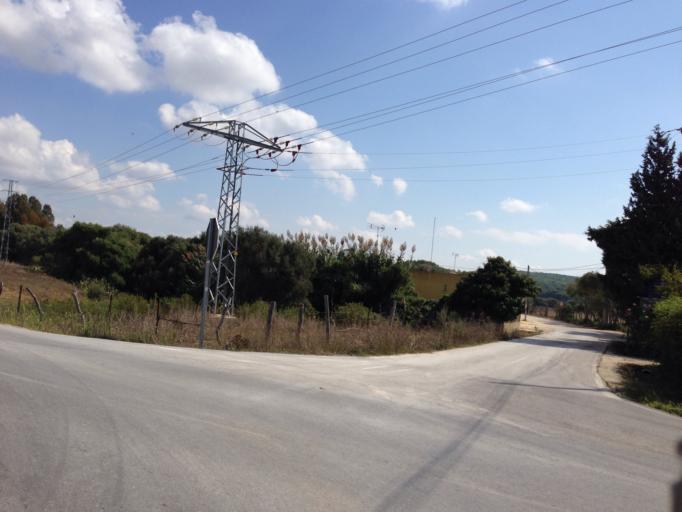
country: ES
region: Andalusia
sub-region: Provincia de Cadiz
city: Vejer de la Frontera
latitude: 36.2078
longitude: -6.0355
